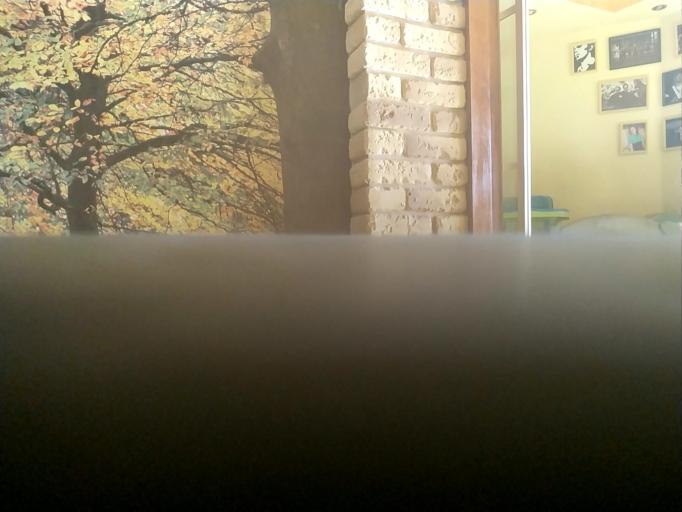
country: RU
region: Smolensk
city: Temkino
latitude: 55.0913
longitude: 34.9030
